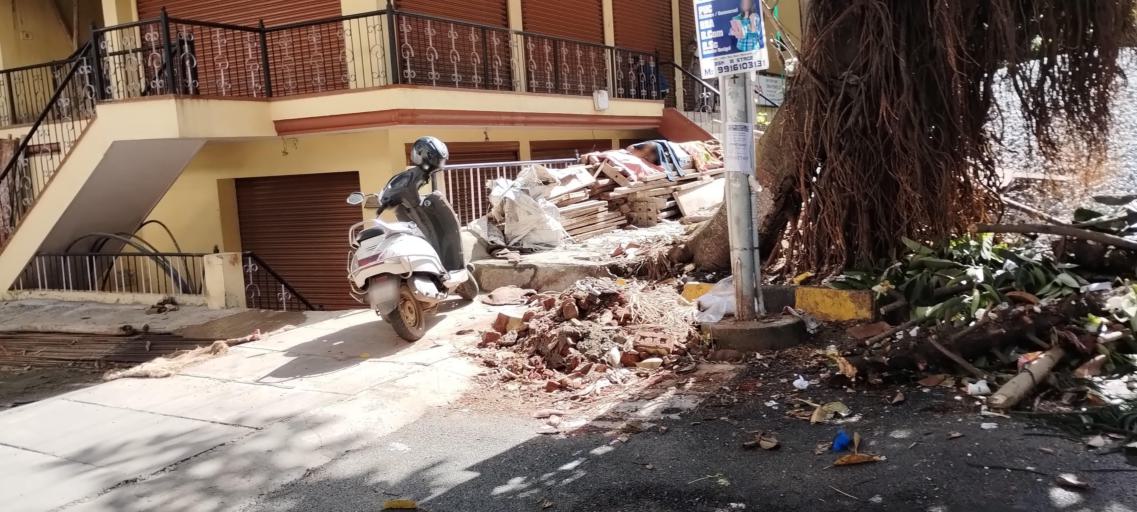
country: IN
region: Karnataka
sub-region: Bangalore Urban
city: Bangalore
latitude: 12.9410
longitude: 77.5392
